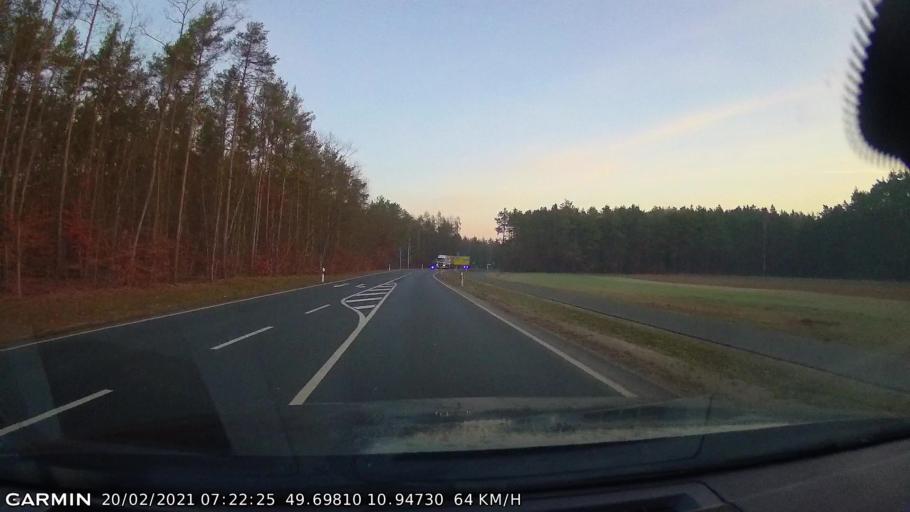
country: DE
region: Bavaria
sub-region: Regierungsbezirk Mittelfranken
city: Hemhofen
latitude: 49.6981
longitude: 10.9473
